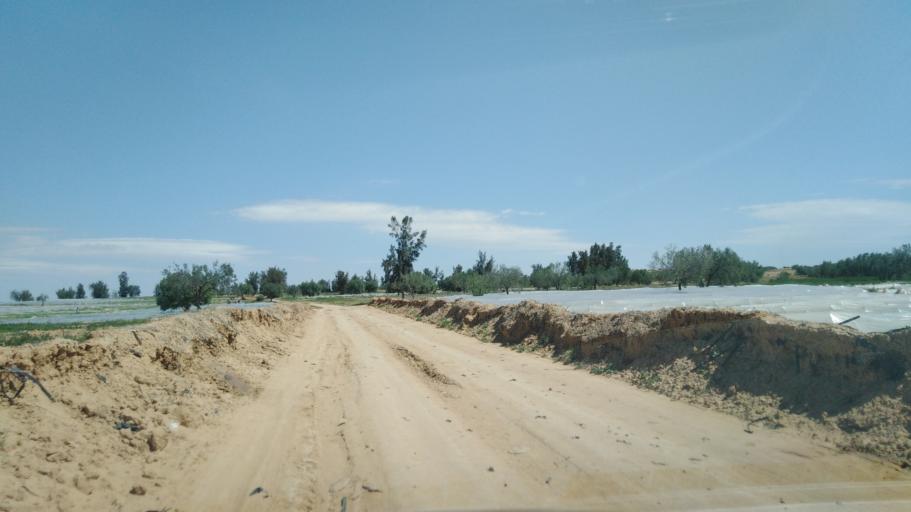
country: TN
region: Safaqis
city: Sfax
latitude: 34.7686
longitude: 10.5275
